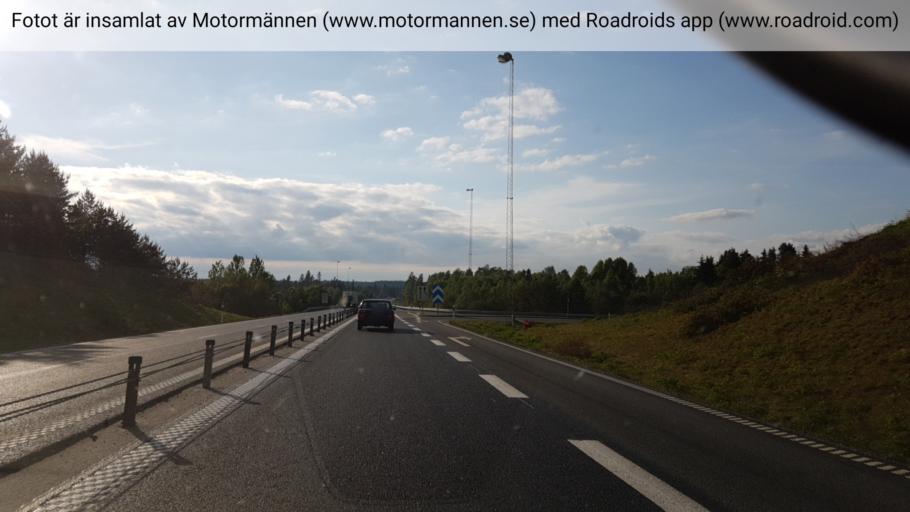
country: SE
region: Joenkoeping
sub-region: Nassjo Kommun
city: Malmback
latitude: 57.6854
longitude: 14.4648
